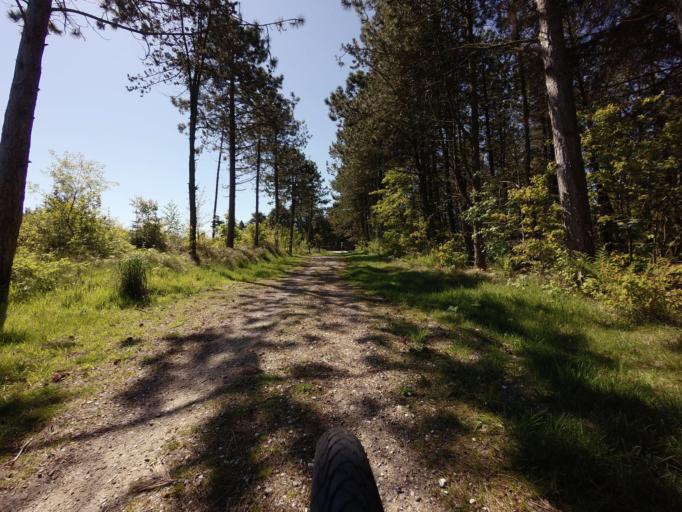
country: DK
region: North Denmark
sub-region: Jammerbugt Kommune
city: Pandrup
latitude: 57.2878
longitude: 9.6423
